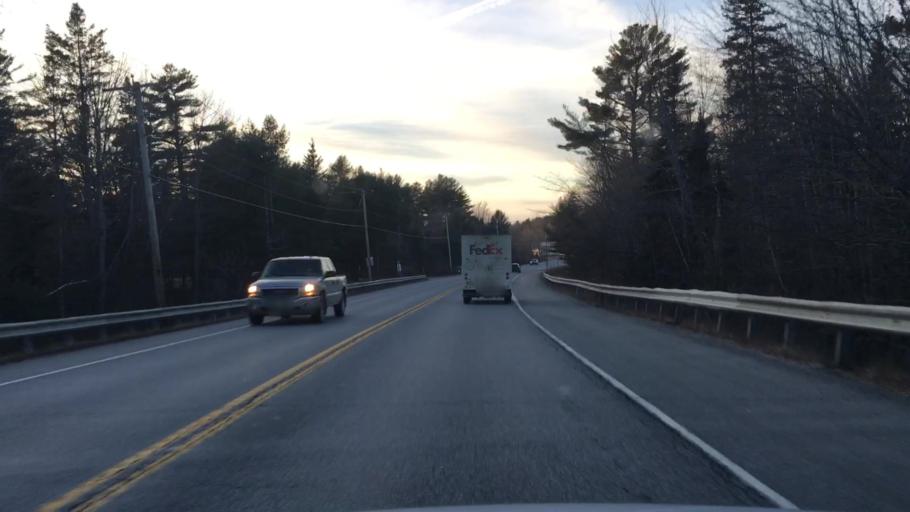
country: US
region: Maine
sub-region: Penobscot County
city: Holden
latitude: 44.7547
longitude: -68.6804
